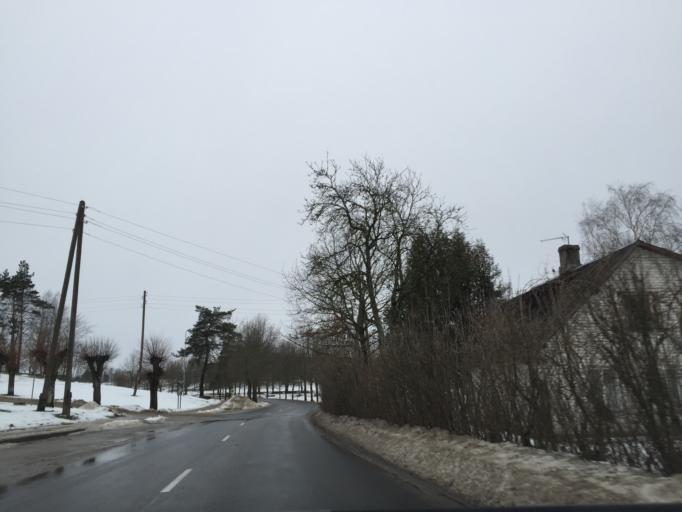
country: LV
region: Krimulda
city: Ragana
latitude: 57.1814
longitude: 24.7097
